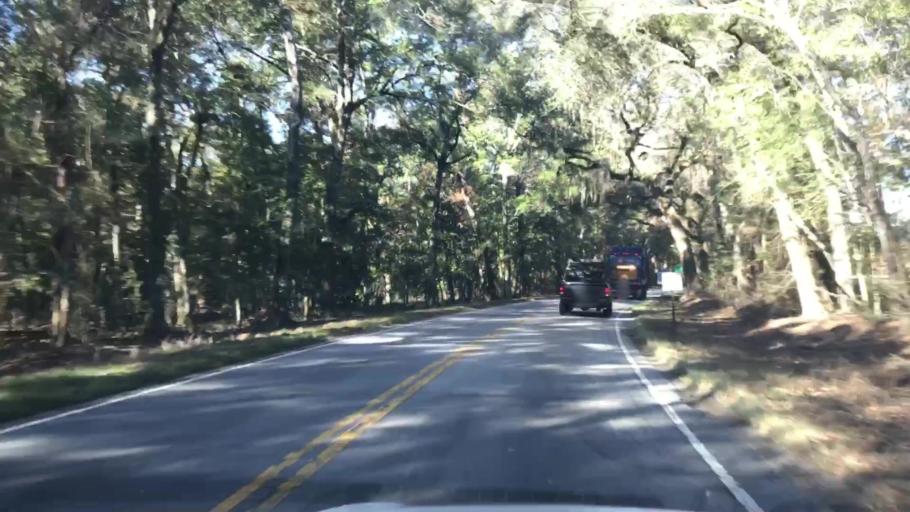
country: US
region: South Carolina
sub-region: Berkeley County
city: Ladson
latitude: 32.8903
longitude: -80.1280
